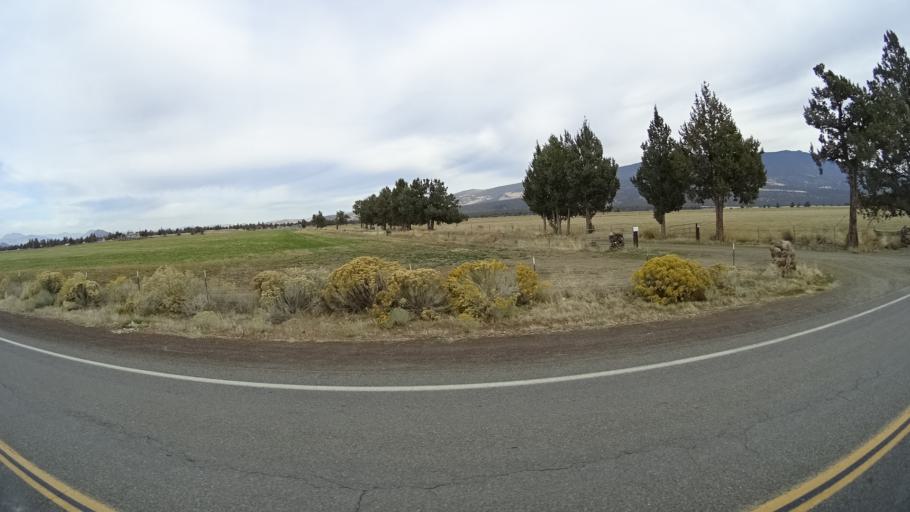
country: US
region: California
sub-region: Siskiyou County
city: Weed
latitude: 41.5969
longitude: -122.3410
